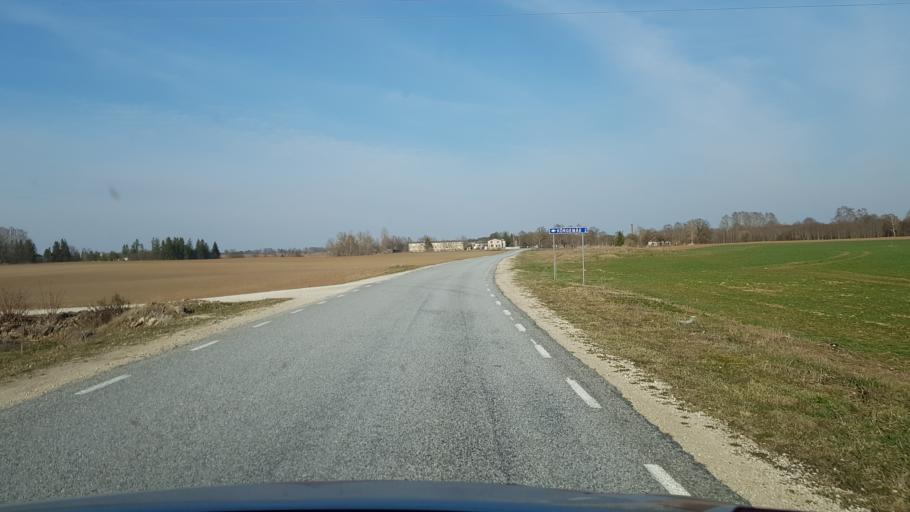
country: EE
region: Laeaene-Virumaa
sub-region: Rakvere linn
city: Rakvere
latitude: 59.3264
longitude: 26.2739
